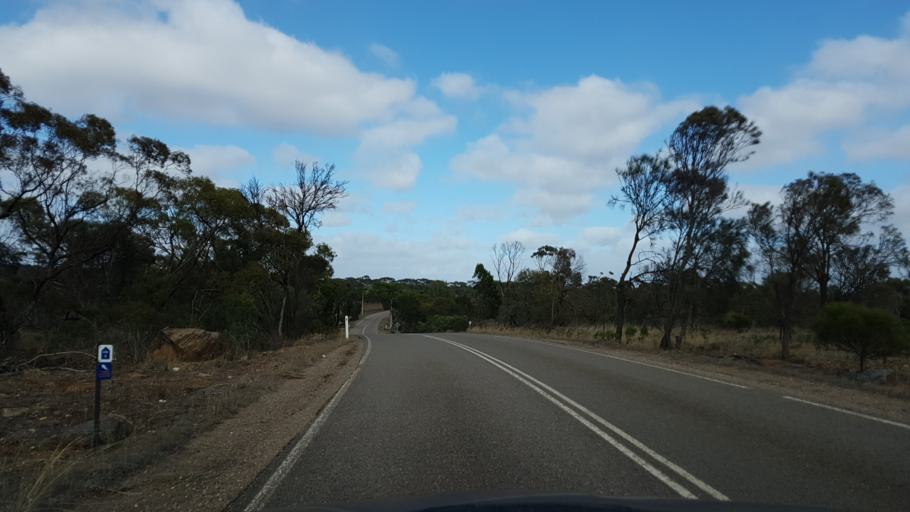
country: AU
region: South Australia
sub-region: Murray Bridge
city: Murray Bridge
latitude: -35.1127
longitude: 139.2215
